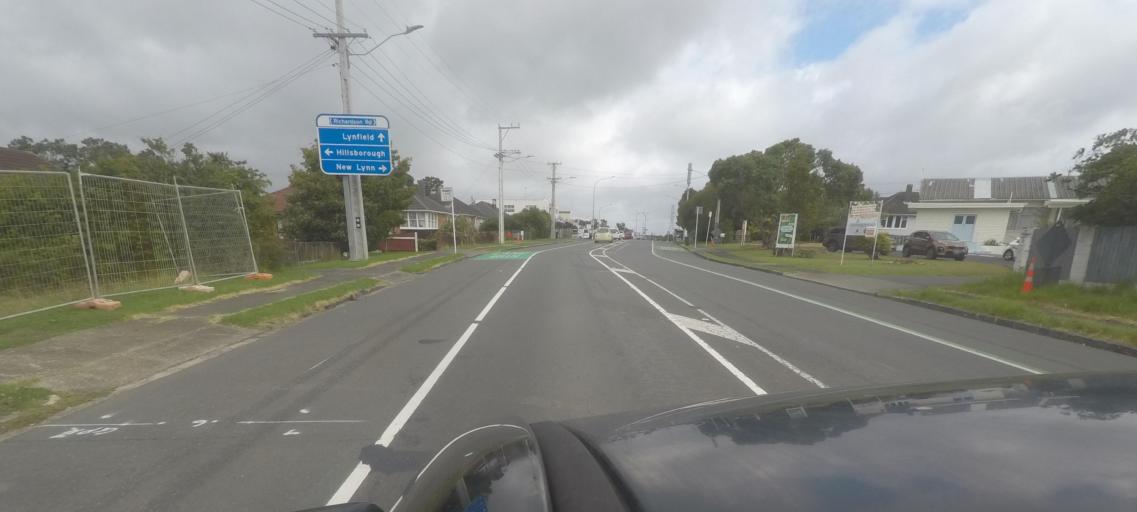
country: NZ
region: Auckland
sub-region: Auckland
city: Auckland
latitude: -36.9190
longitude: 174.7371
